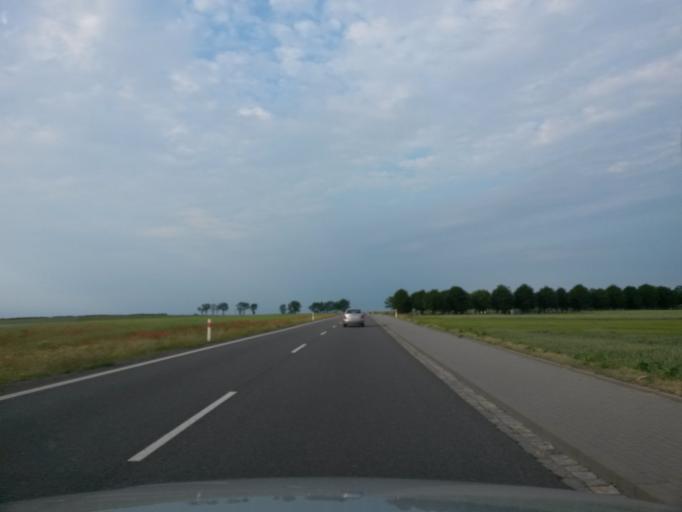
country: PL
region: Lower Silesian Voivodeship
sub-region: Powiat swidnicki
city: Zarow
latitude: 51.0127
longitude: 16.5524
